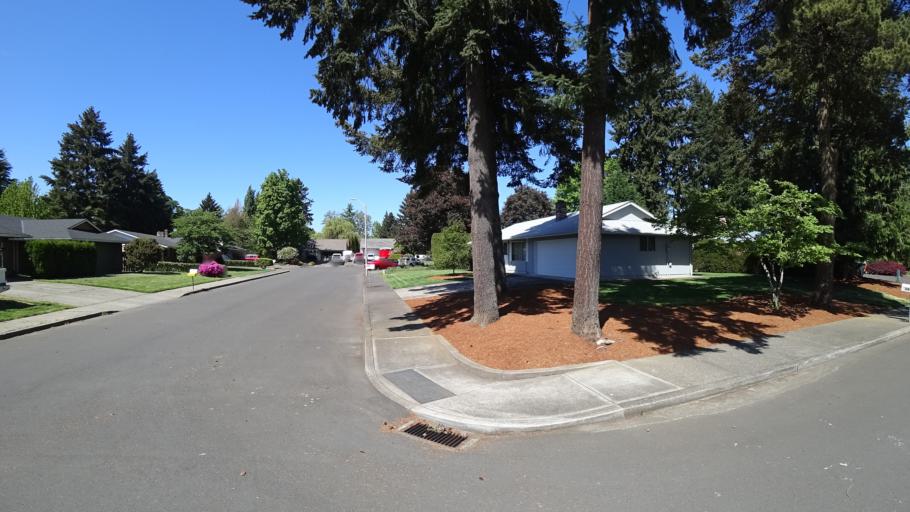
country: US
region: Oregon
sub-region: Washington County
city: Hillsboro
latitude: 45.5177
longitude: -122.9478
